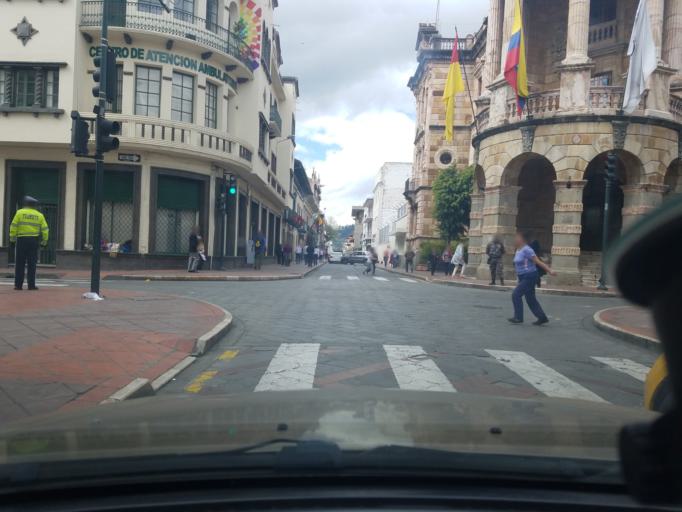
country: EC
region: Azuay
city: Cuenca
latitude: -2.8972
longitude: -79.0030
